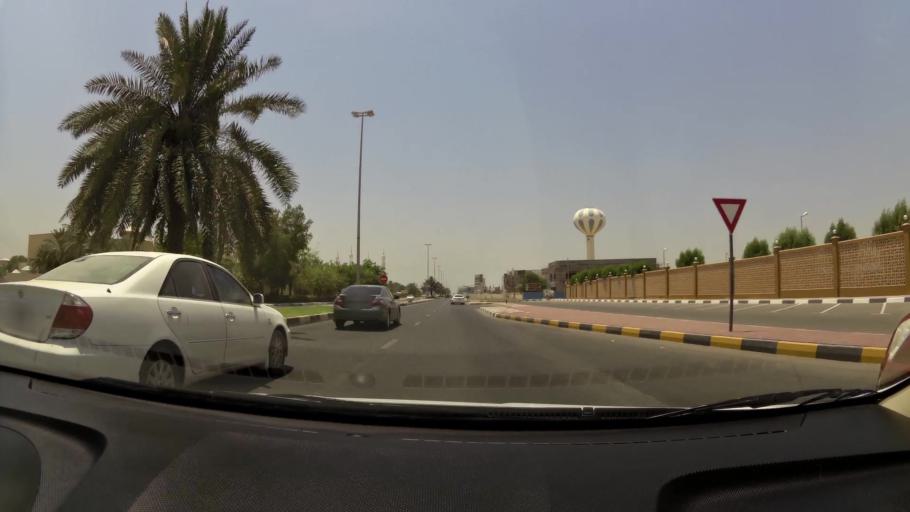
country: AE
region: Ajman
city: Ajman
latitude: 25.4160
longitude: 55.4946
